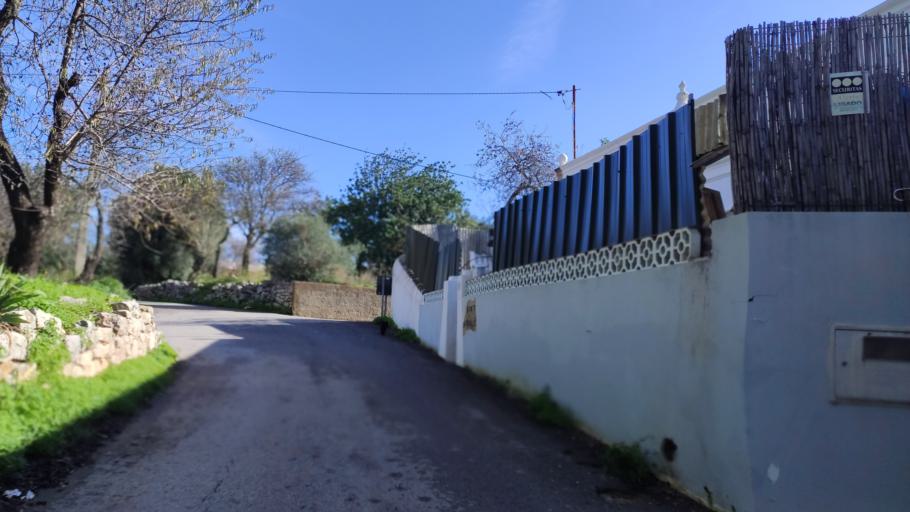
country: PT
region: Faro
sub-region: Sao Bras de Alportel
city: Sao Bras de Alportel
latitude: 37.1502
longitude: -7.8739
